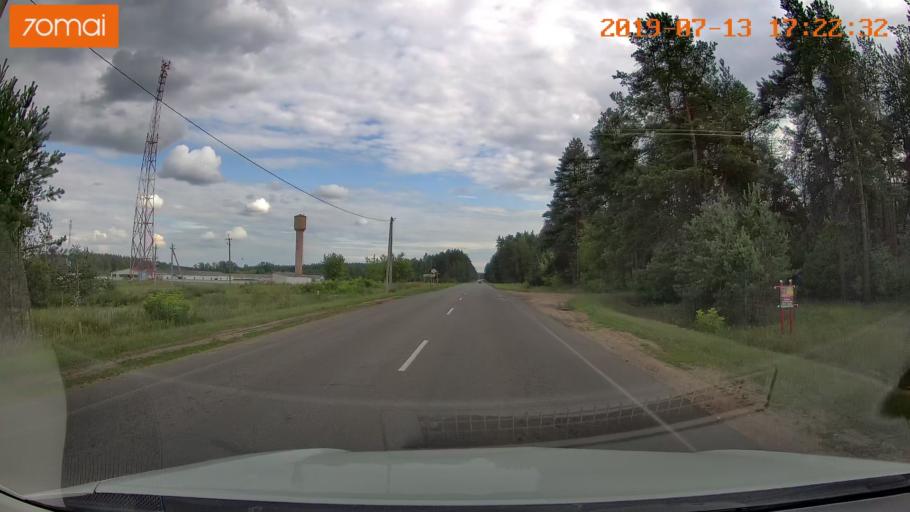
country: BY
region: Mogilev
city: Babruysk
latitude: 53.2701
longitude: 29.2346
